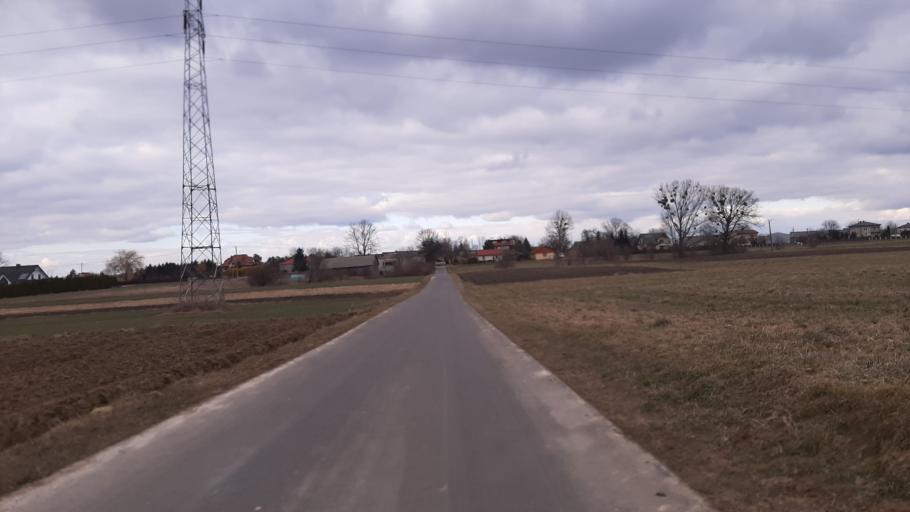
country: PL
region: Lublin Voivodeship
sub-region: Powiat lubelski
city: Jastkow
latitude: 51.3504
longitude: 22.3927
